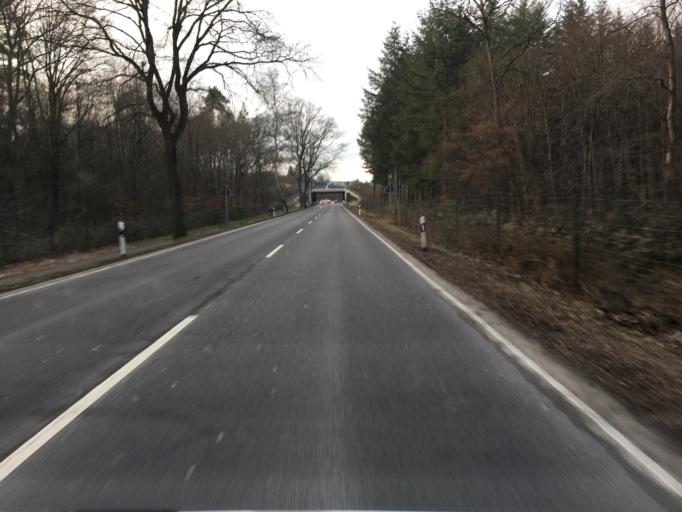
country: DE
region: North Rhine-Westphalia
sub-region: Regierungsbezirk Koln
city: Rath
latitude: 50.9108
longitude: 7.1264
